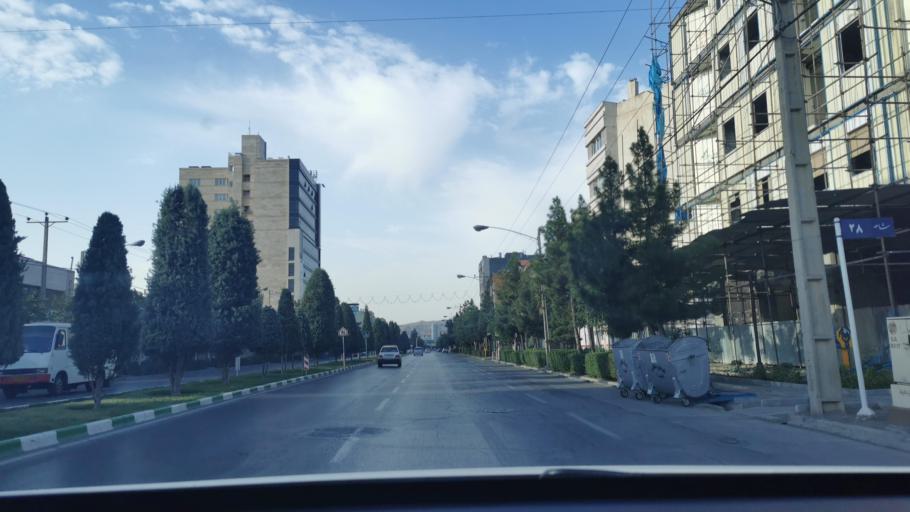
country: IR
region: Razavi Khorasan
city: Mashhad
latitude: 36.3544
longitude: 59.5016
